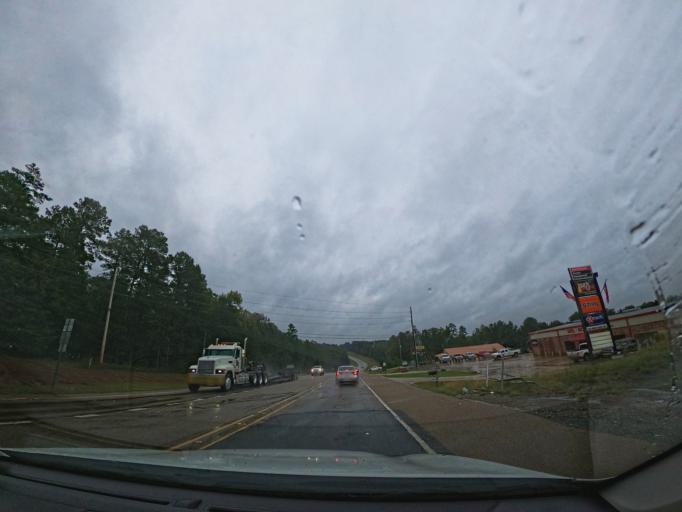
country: US
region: Louisiana
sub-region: Webster Parish
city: Minden
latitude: 32.6012
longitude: -93.2500
